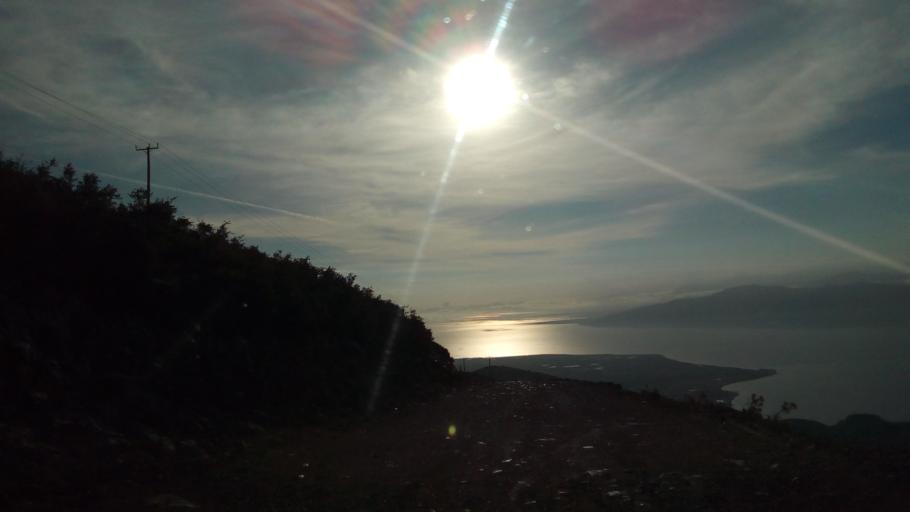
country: GR
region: West Greece
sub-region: Nomos Aitolias kai Akarnanias
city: Nafpaktos
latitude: 38.4199
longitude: 21.8039
